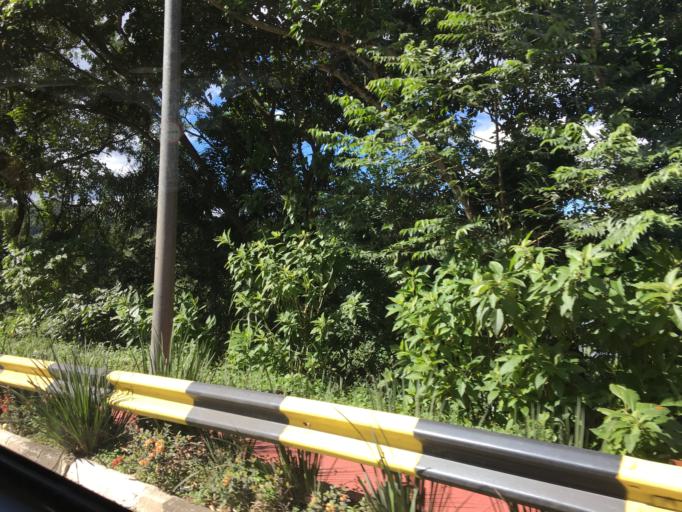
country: BR
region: Sao Paulo
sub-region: Santana De Parnaiba
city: Santana de Parnaiba
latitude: -23.4459
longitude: -46.9123
